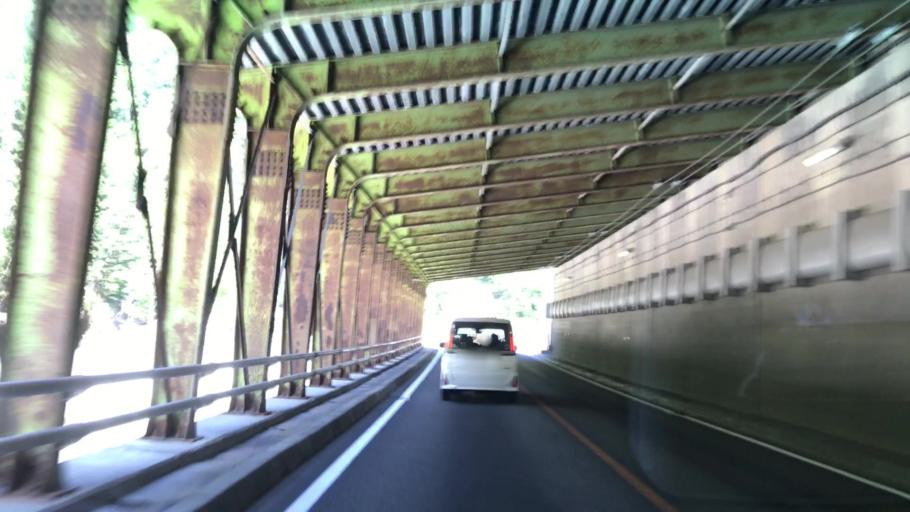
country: JP
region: Hokkaido
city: Shimo-furano
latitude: 42.9440
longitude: 142.5986
